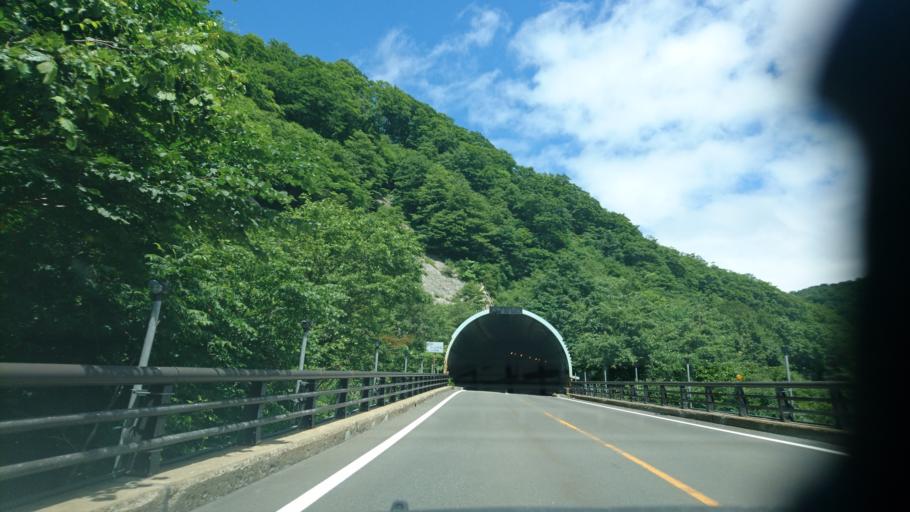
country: JP
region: Iwate
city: Shizukuishi
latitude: 39.6910
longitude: 140.7966
